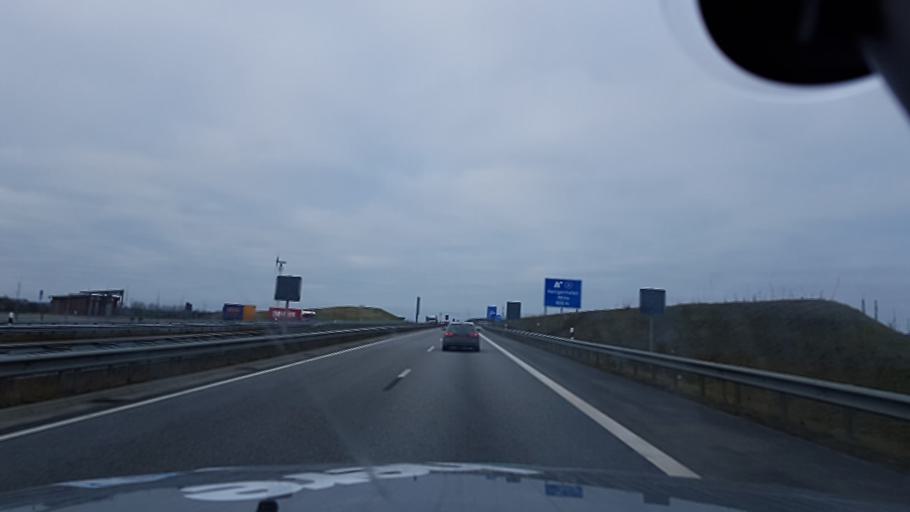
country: DE
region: Schleswig-Holstein
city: Heiligenhafen
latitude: 54.3623
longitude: 10.9841
